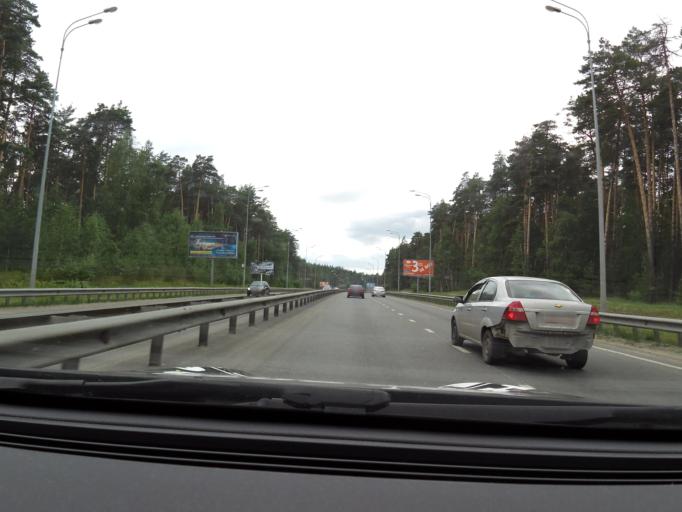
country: RU
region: Tatarstan
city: Staroye Arakchino
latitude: 55.8303
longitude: 48.9956
